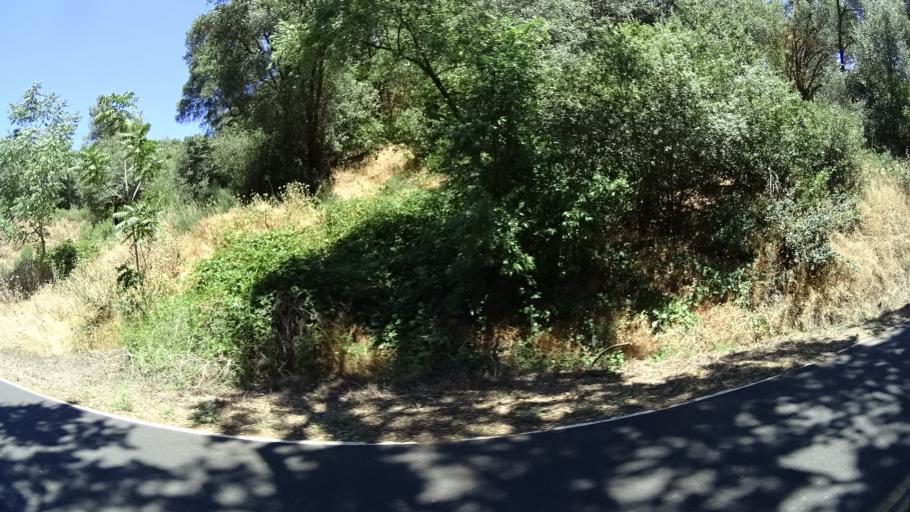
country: US
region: California
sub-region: Calaveras County
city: Angels Camp
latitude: 38.1095
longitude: -120.5209
